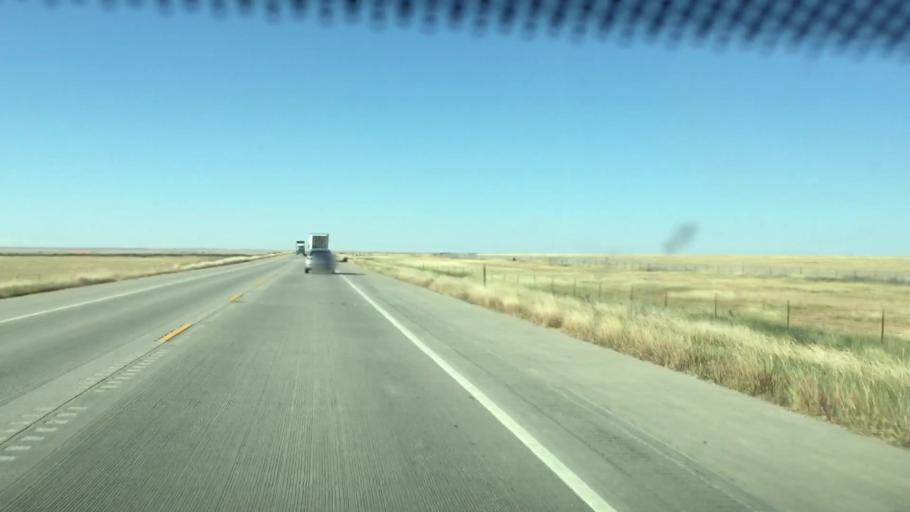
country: US
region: Colorado
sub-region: Kiowa County
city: Eads
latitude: 38.3578
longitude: -102.7179
